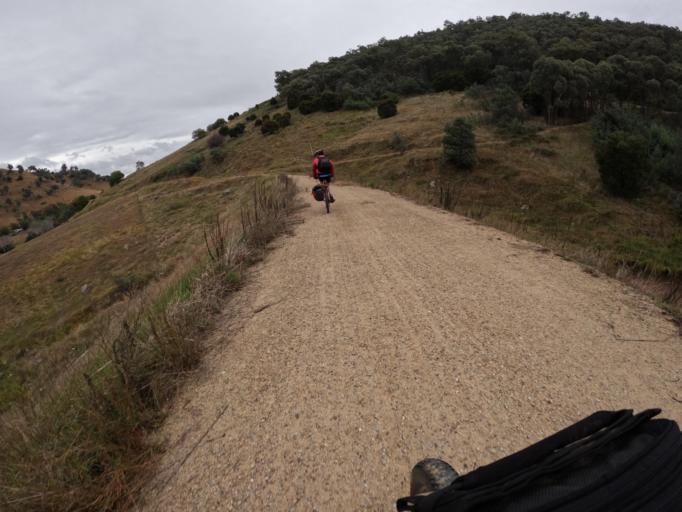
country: AU
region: New South Wales
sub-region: Albury Municipality
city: East Albury
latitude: -36.1845
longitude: 147.3608
